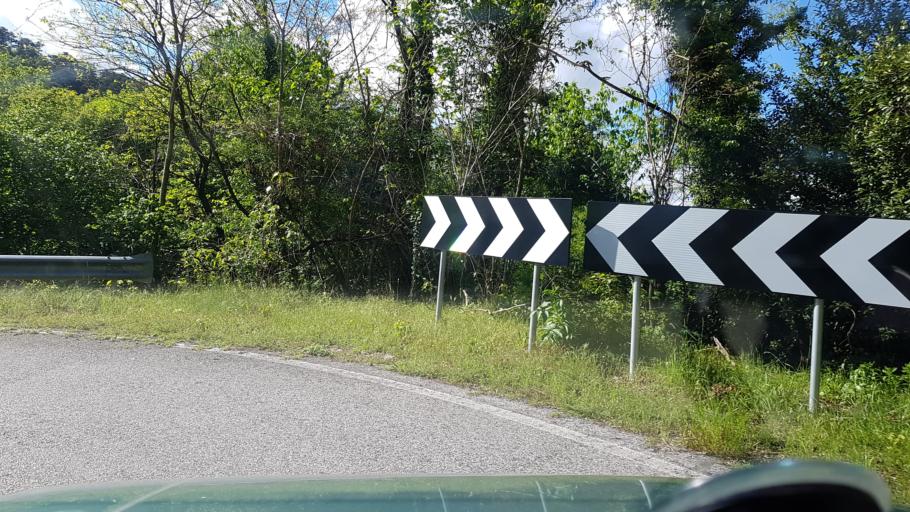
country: SI
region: Miren-Kostanjevica
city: Miren
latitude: 45.8723
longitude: 13.5813
